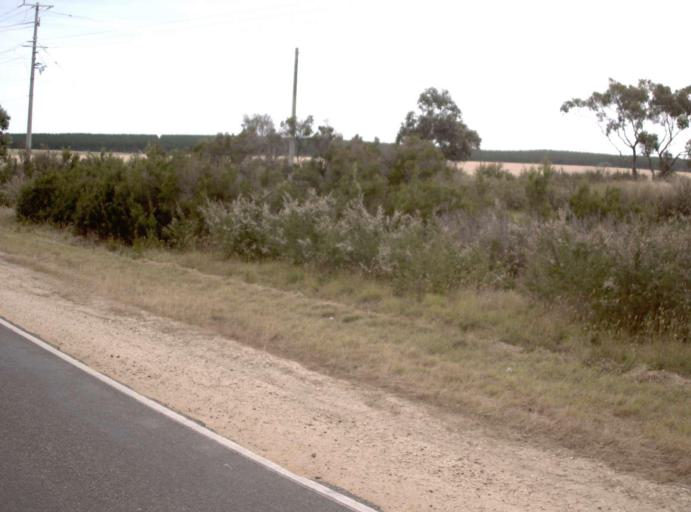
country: AU
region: Victoria
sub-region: Wellington
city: Sale
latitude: -38.1995
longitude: 147.0962
